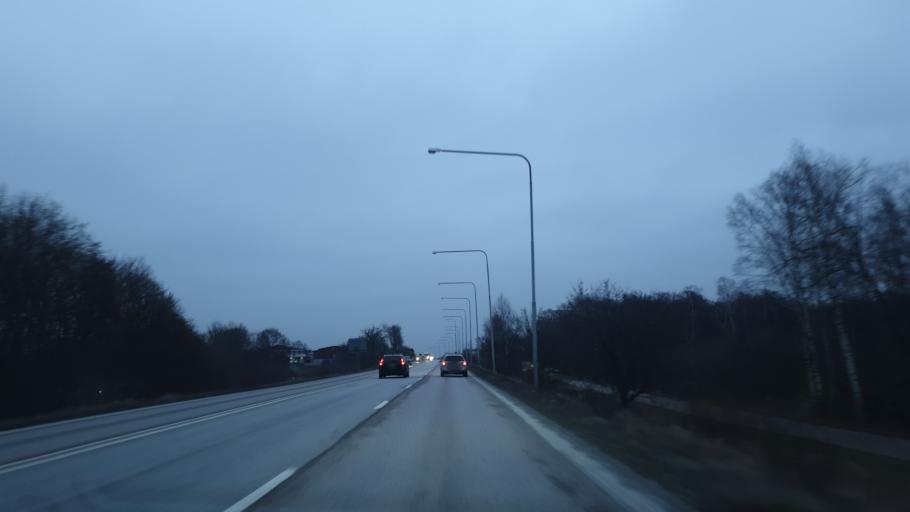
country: SE
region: Blekinge
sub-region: Karlskrona Kommun
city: Karlskrona
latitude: 56.1908
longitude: 15.6234
